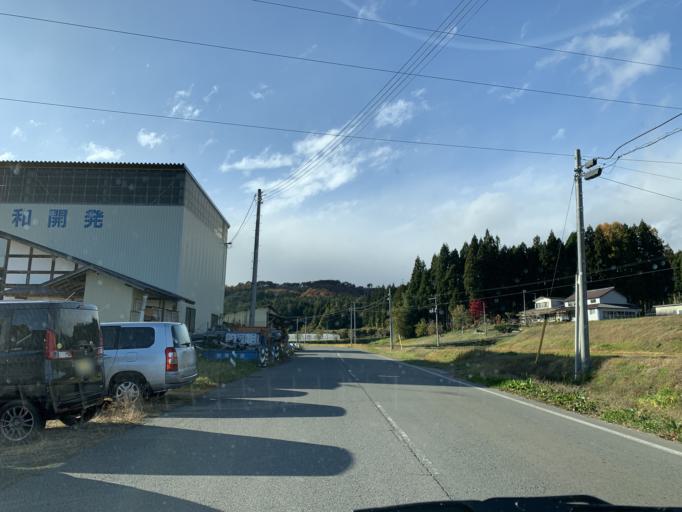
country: JP
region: Iwate
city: Ichinoseki
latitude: 39.0136
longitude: 141.0797
